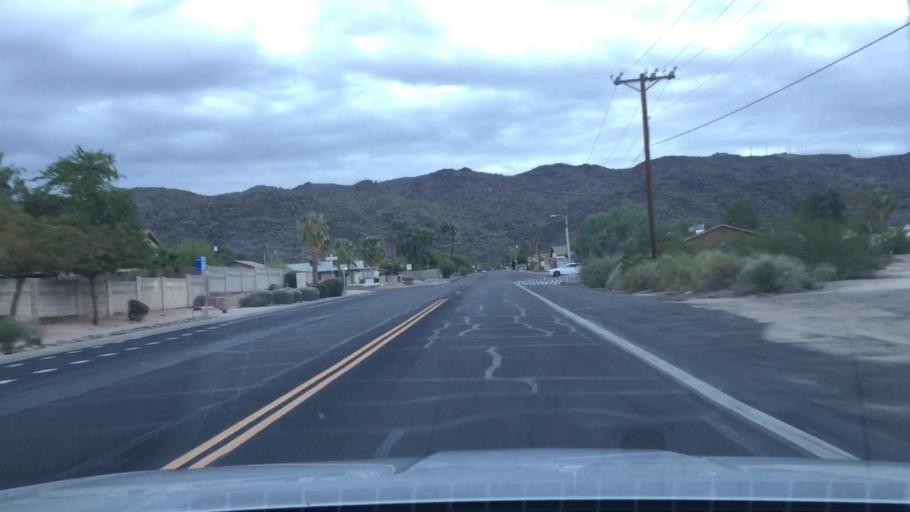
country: US
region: Arizona
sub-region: Maricopa County
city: Phoenix
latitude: 33.3714
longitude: -112.0488
